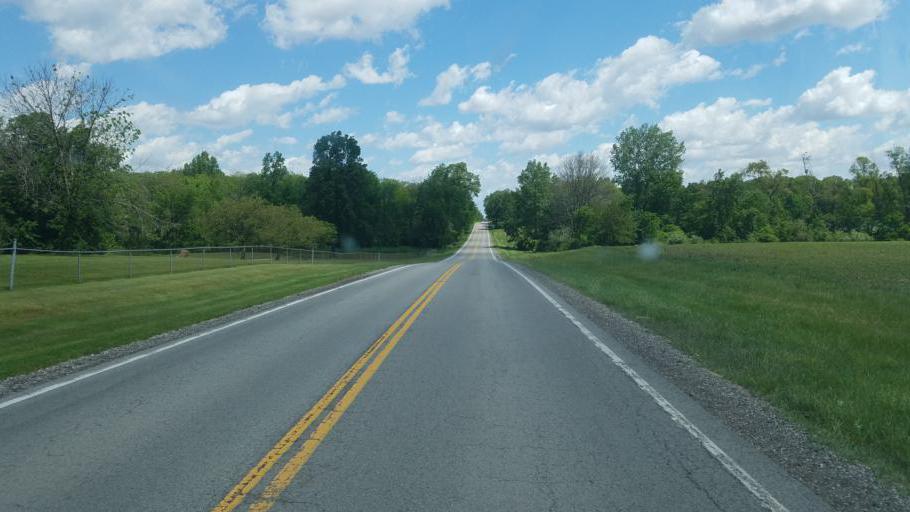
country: US
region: Ohio
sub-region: Huron County
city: Plymouth
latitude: 40.9397
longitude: -82.7252
